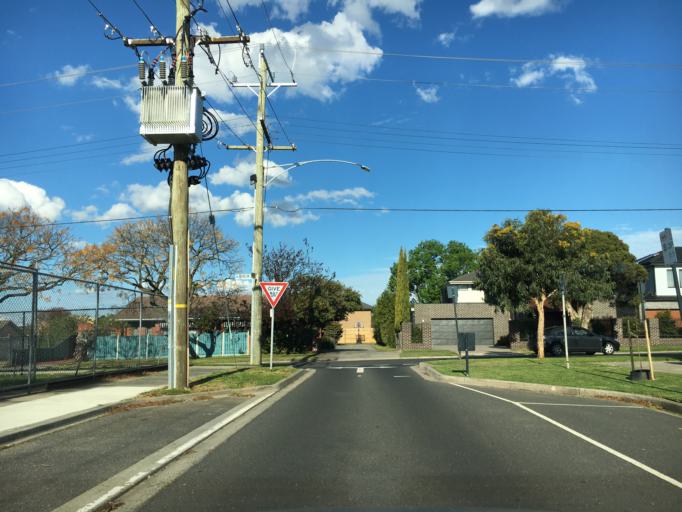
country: AU
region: Victoria
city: Clayton
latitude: -37.9005
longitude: 145.1098
